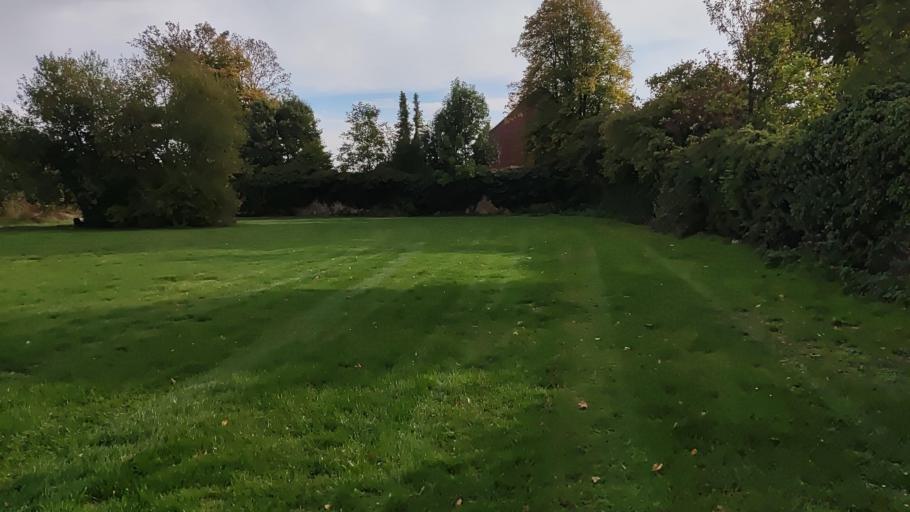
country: BE
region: Wallonia
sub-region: Province du Brabant Wallon
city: Jodoigne
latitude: 50.7269
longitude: 4.8695
